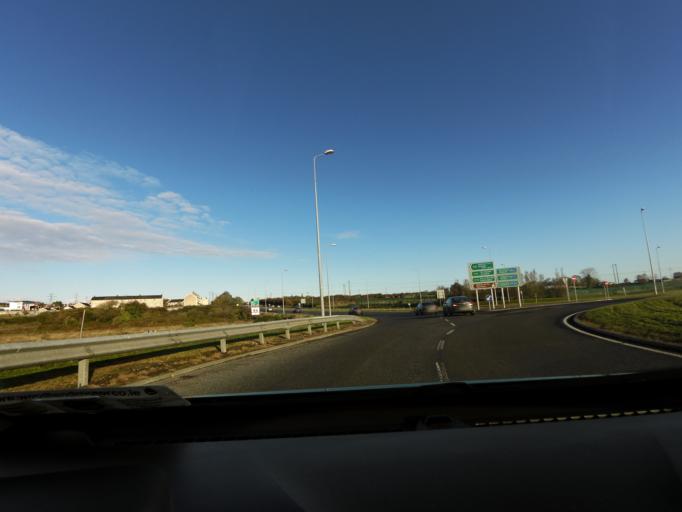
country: IE
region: Connaught
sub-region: County Galway
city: Oranmore
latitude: 53.2854
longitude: -8.9799
